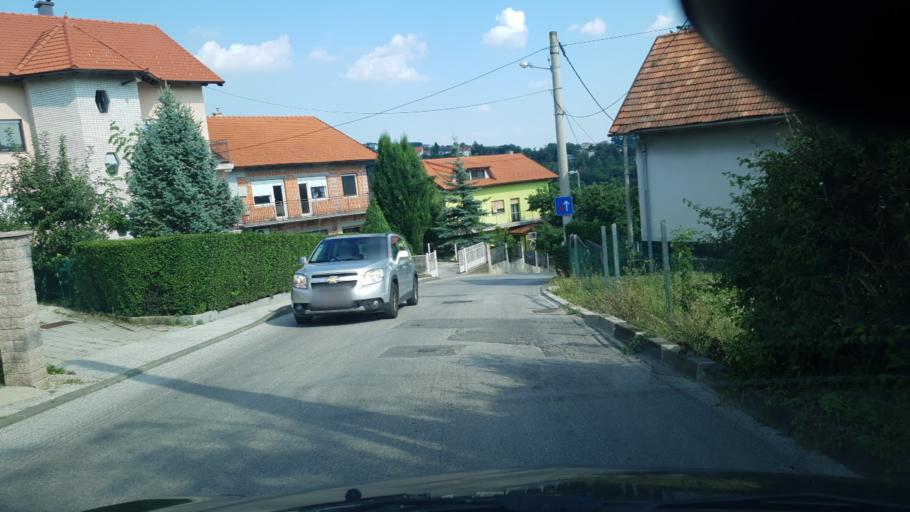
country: HR
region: Grad Zagreb
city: Stenjevec
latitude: 45.8401
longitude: 15.9176
